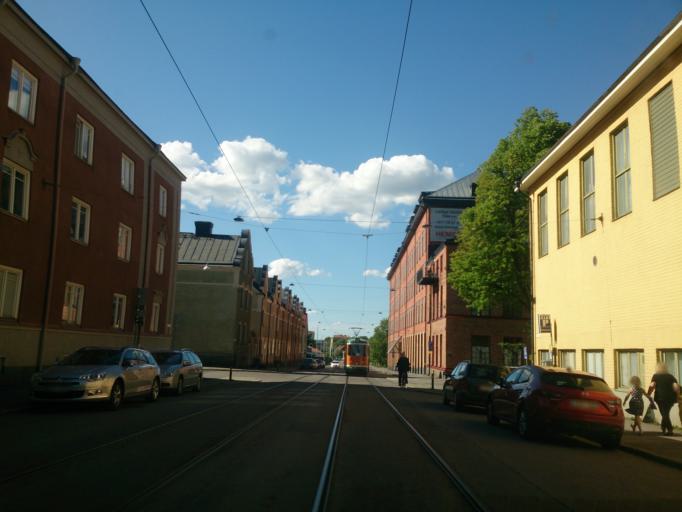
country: SE
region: OEstergoetland
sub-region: Norrkopings Kommun
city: Norrkoping
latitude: 58.5944
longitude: 16.1679
